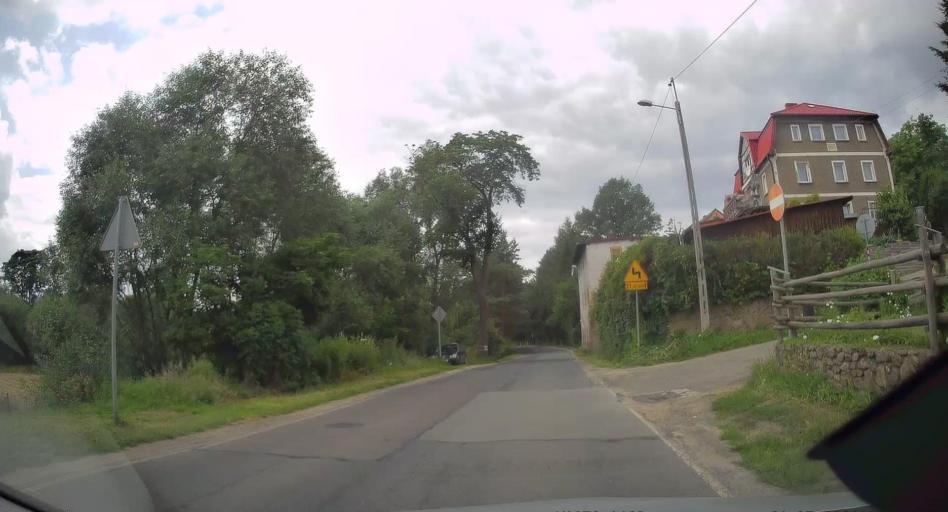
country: PL
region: Lower Silesian Voivodeship
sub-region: Powiat kamiennogorski
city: Marciszow
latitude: 50.8428
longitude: 16.0312
